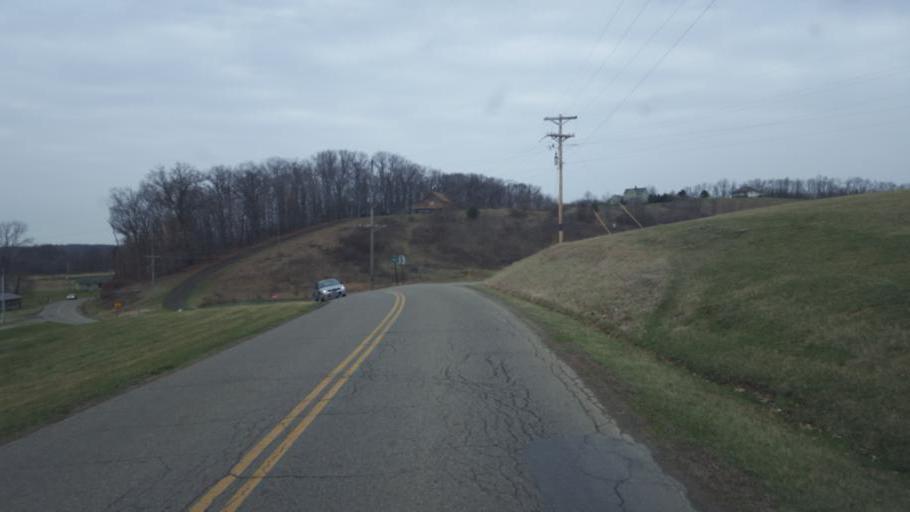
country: US
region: Ohio
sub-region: Knox County
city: Fredericktown
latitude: 40.5241
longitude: -82.4863
